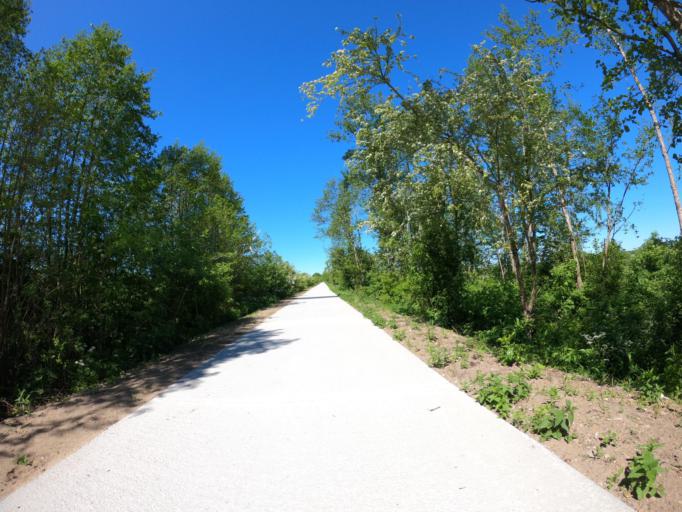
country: PL
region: Pomeranian Voivodeship
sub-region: Powiat slupski
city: Ustka
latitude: 54.5127
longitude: 16.7551
